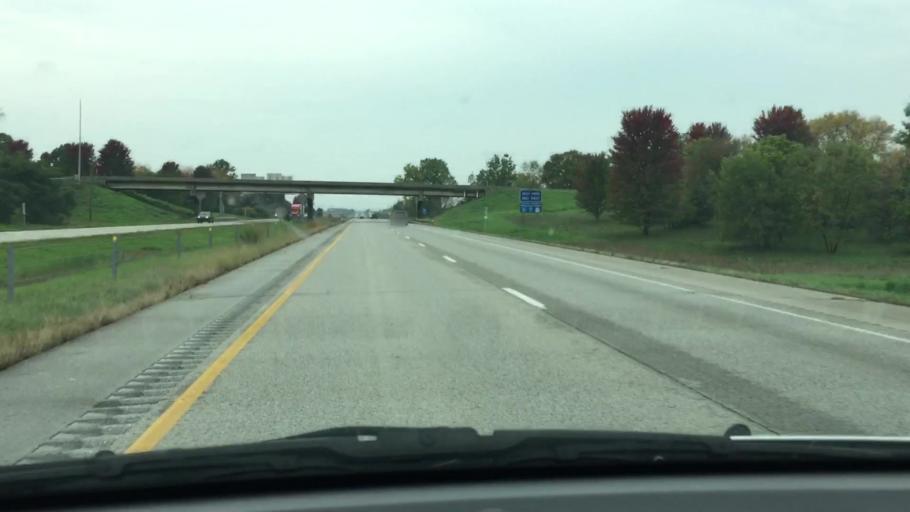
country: US
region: Iowa
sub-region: Johnson County
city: Tiffin
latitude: 41.6940
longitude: -91.6647
